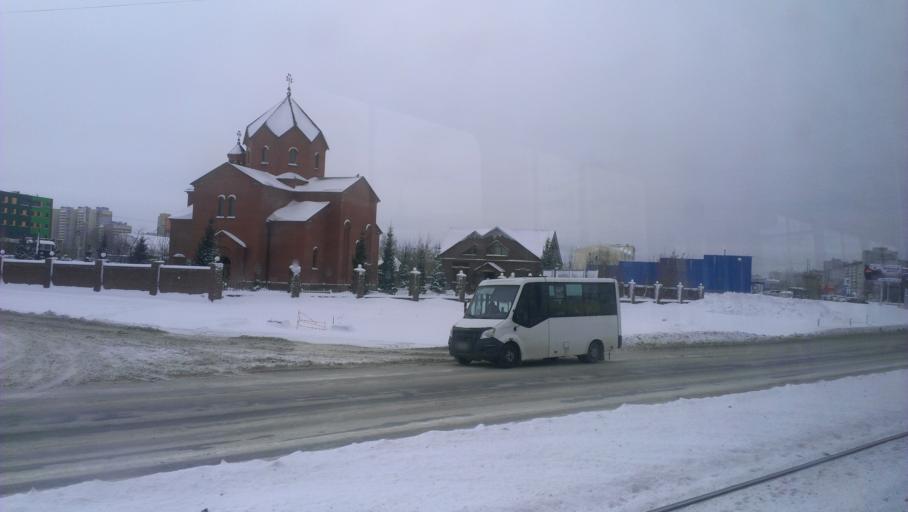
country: RU
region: Altai Krai
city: Novosilikatnyy
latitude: 53.3313
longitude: 83.6671
